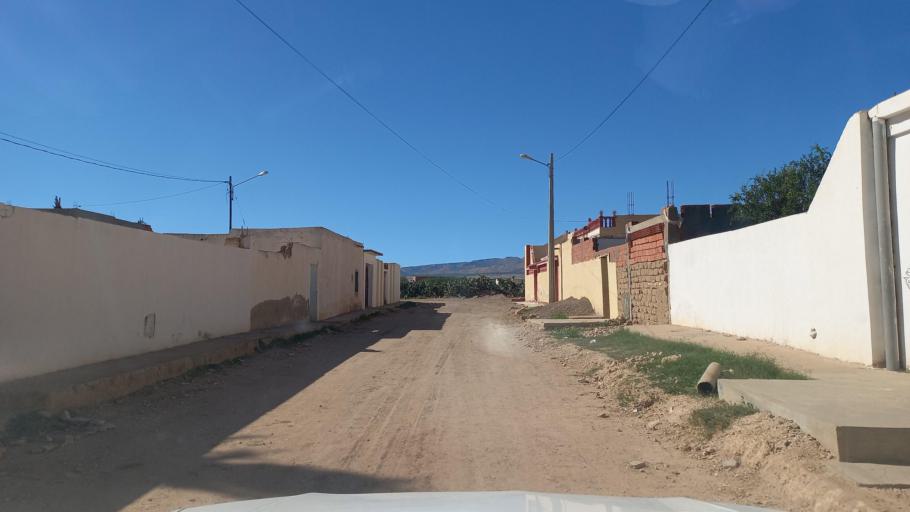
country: TN
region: Al Qasrayn
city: Sbiba
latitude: 35.3955
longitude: 9.1182
